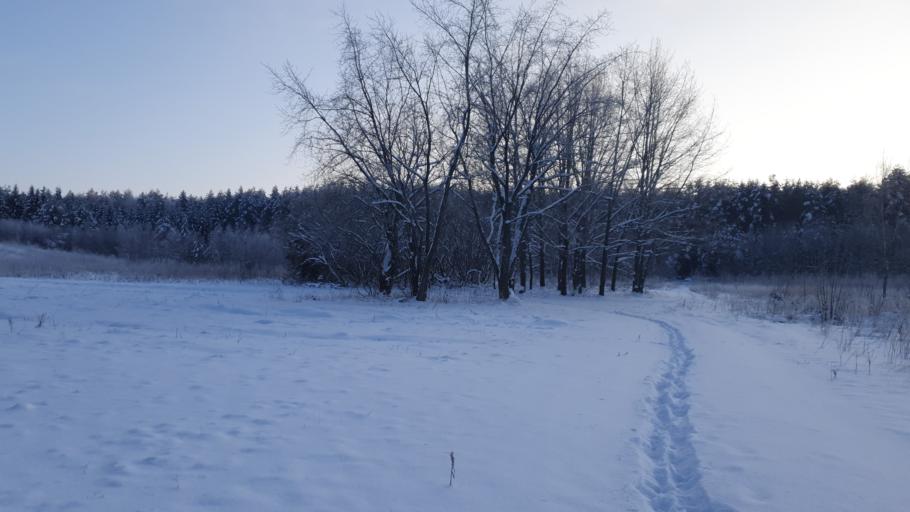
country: LT
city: Skaidiskes
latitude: 54.6477
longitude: 25.4240
